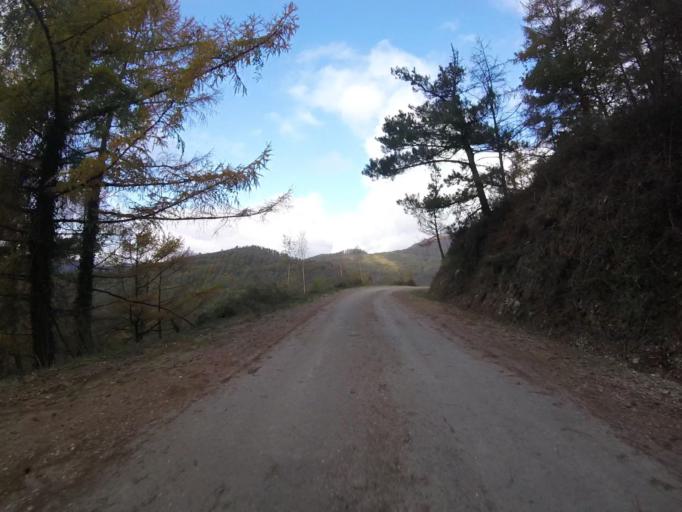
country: ES
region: Navarre
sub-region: Provincia de Navarra
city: Goizueta
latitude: 43.2169
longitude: -1.8517
